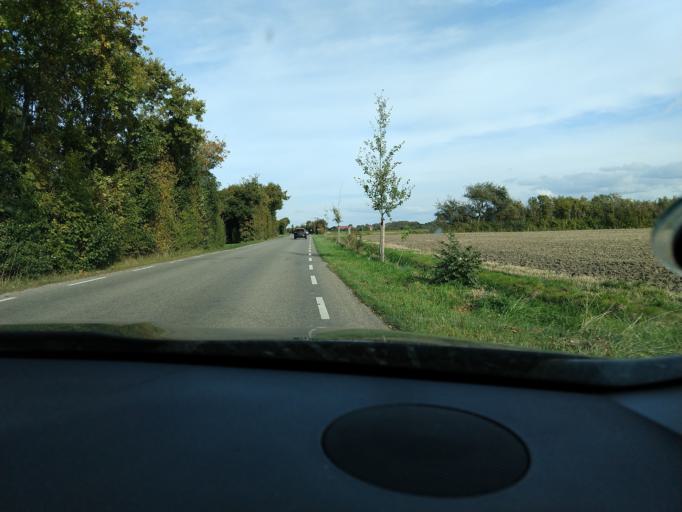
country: NL
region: Zeeland
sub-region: Gemeente Vlissingen
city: Vlissingen
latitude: 51.5314
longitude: 3.4580
